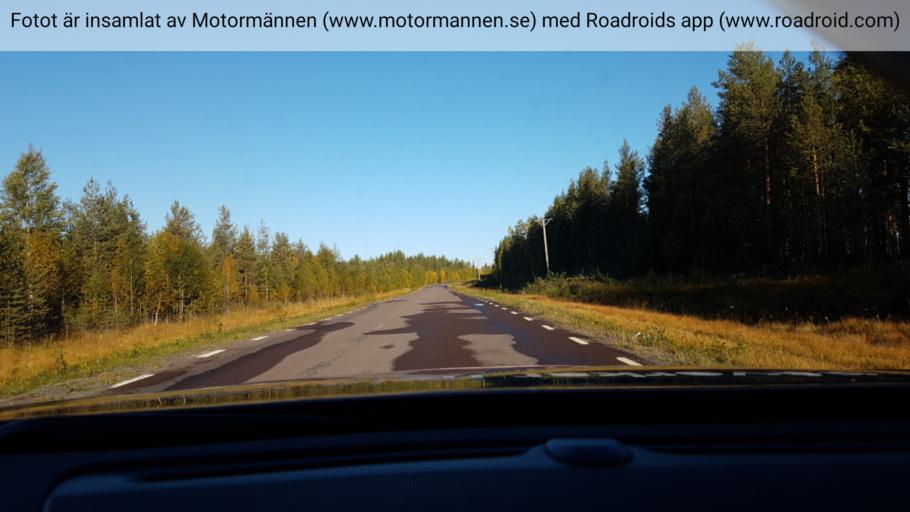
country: SE
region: Norrbotten
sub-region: Bodens Kommun
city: Boden
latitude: 66.0673
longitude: 21.4009
